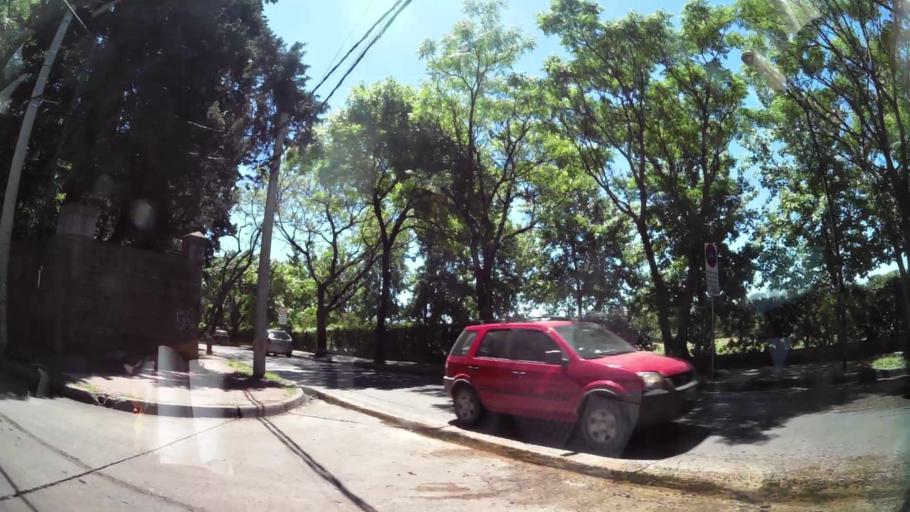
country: AR
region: Buenos Aires
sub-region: Partido de San Isidro
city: San Isidro
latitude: -34.4569
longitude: -58.5187
